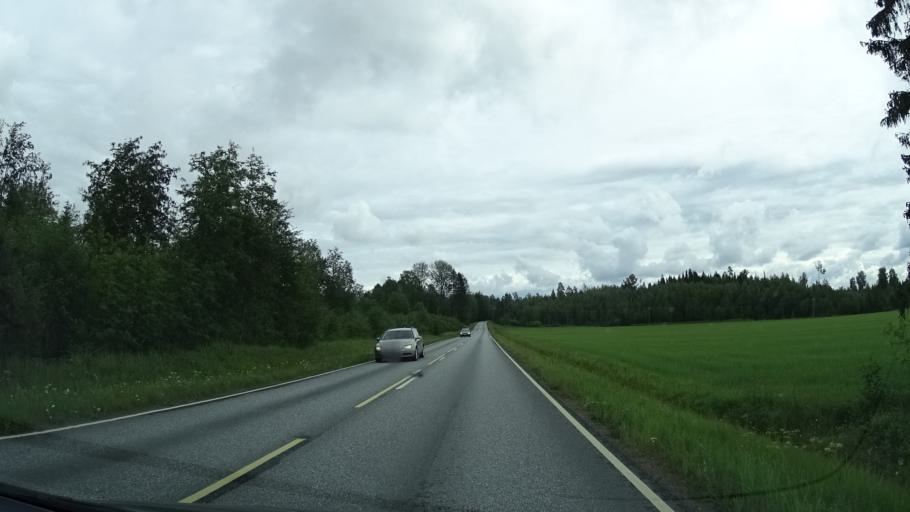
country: FI
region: Pirkanmaa
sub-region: Etelae-Pirkanmaa
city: Urjala
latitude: 61.0923
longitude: 23.3857
